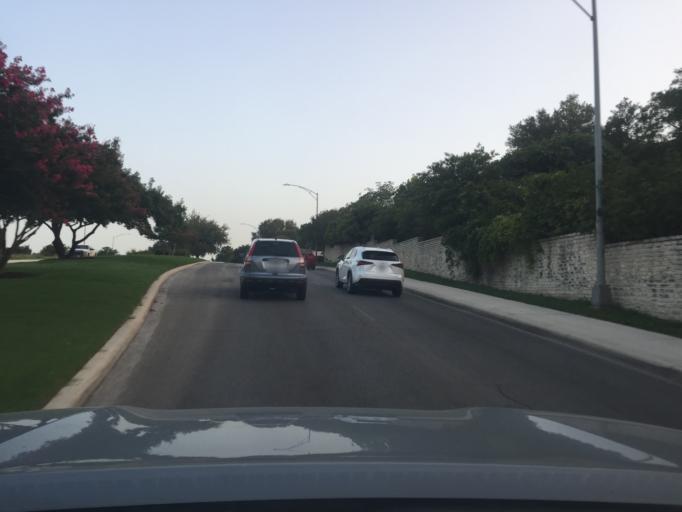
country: US
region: Texas
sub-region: Bexar County
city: Hollywood Park
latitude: 29.6367
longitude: -98.4958
